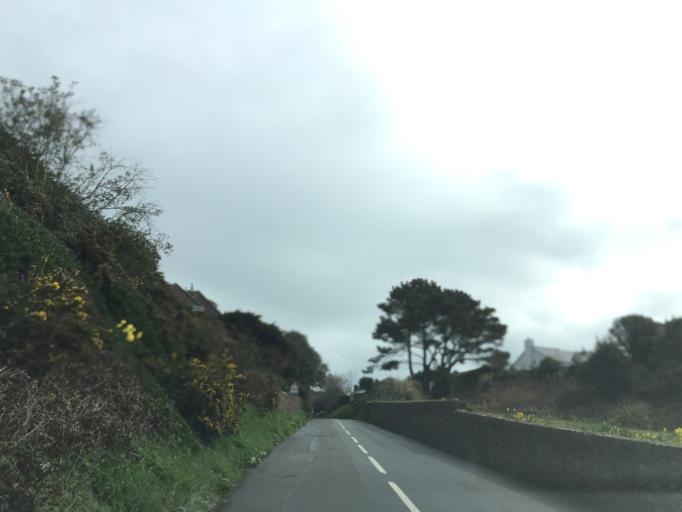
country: JE
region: St Helier
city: Saint Helier
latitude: 49.1846
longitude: -2.2292
